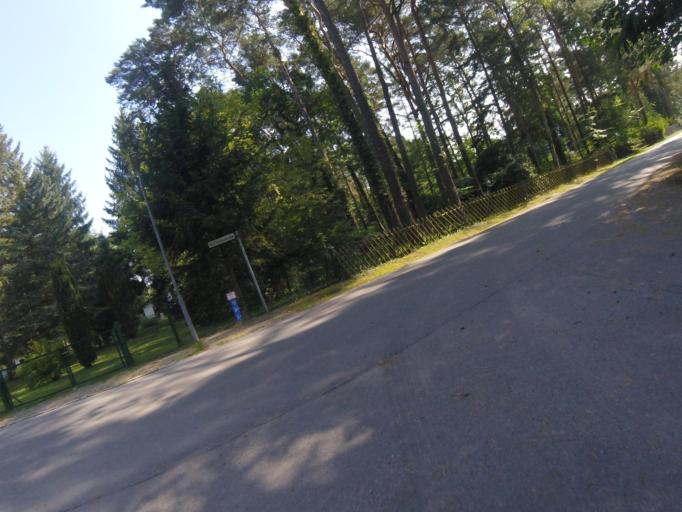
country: DE
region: Brandenburg
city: Bestensee
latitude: 52.2634
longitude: 13.7455
